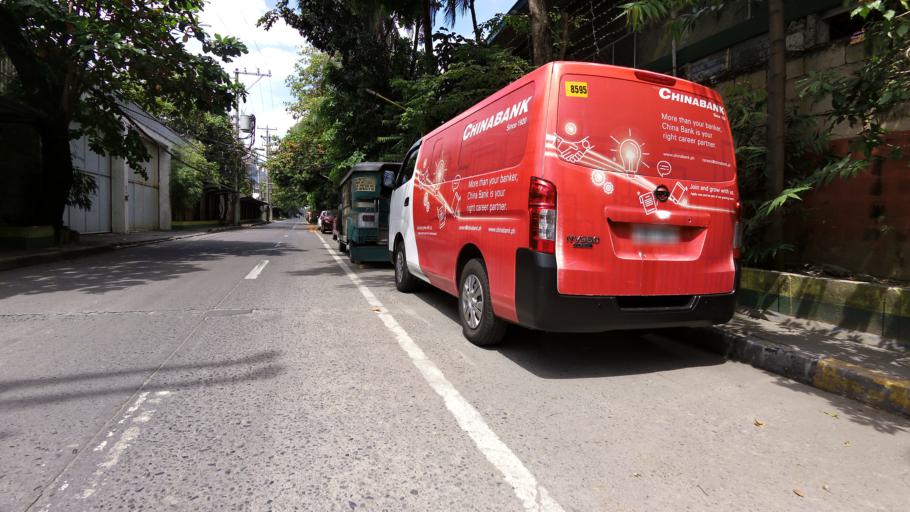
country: PH
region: Metro Manila
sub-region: Pasig
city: Pasig City
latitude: 14.5799
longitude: 121.0775
